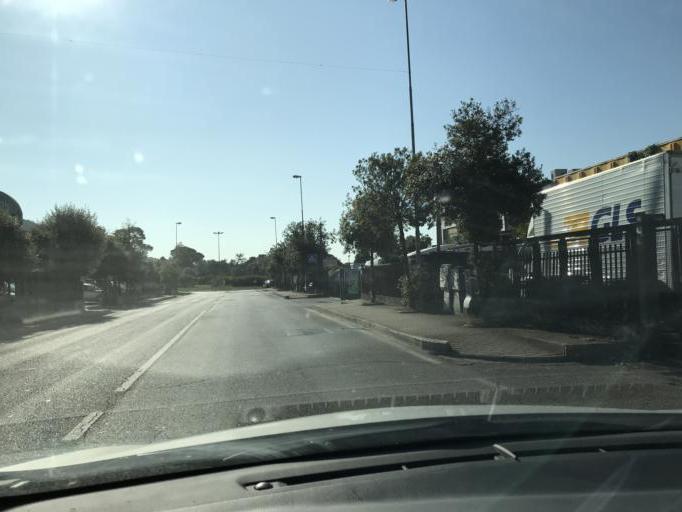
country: IT
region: Umbria
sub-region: Provincia di Perugia
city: Chiugiana-La Commenda
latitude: 43.1002
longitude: 12.3180
